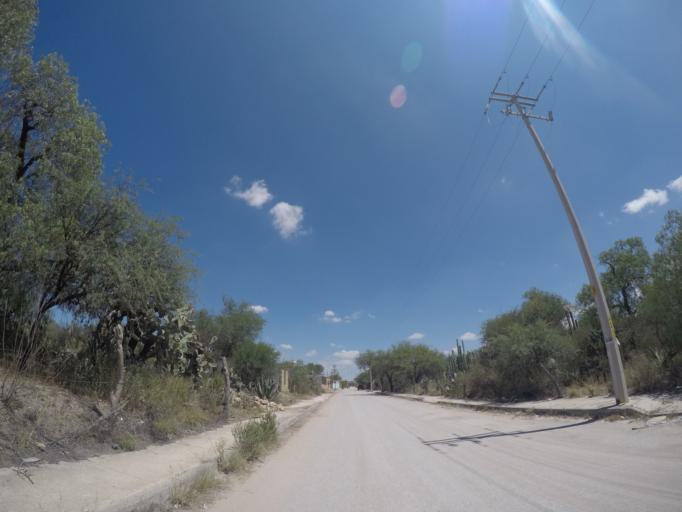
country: MX
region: San Luis Potosi
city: La Pila
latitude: 21.9985
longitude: -100.8983
